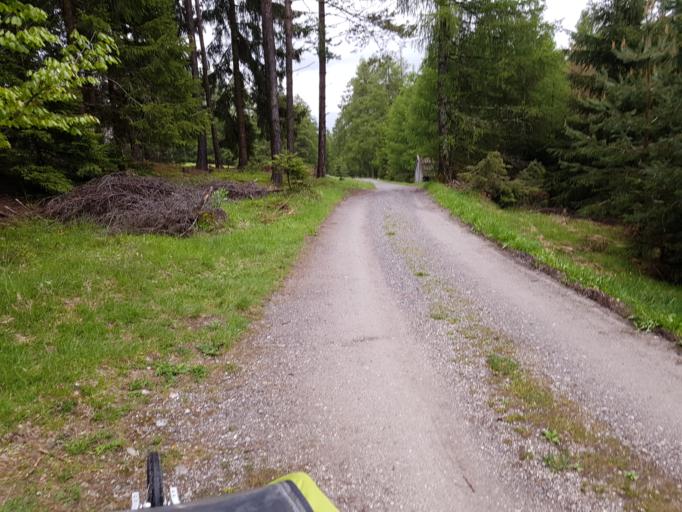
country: AT
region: Tyrol
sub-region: Politischer Bezirk Imst
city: Obsteig
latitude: 47.3100
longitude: 10.9076
